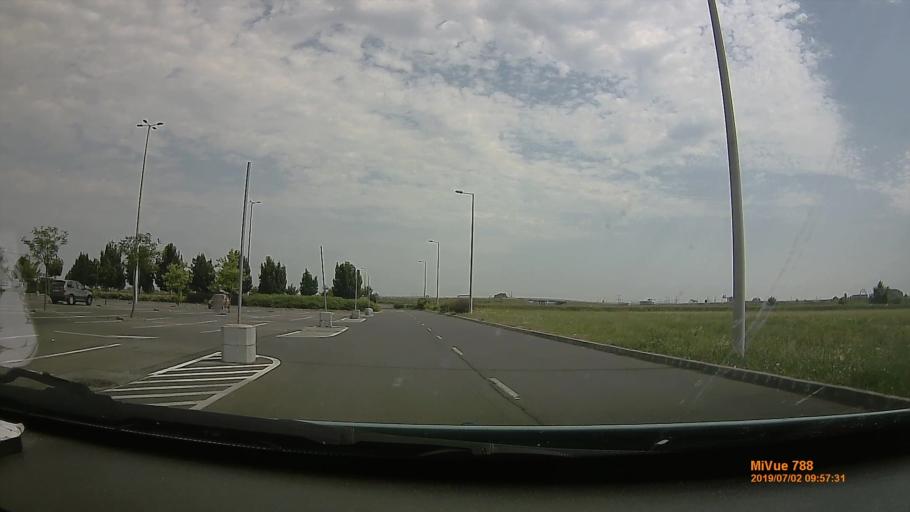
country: HU
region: Borsod-Abauj-Zemplen
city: Felsozsolca
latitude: 48.1082
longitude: 20.8382
